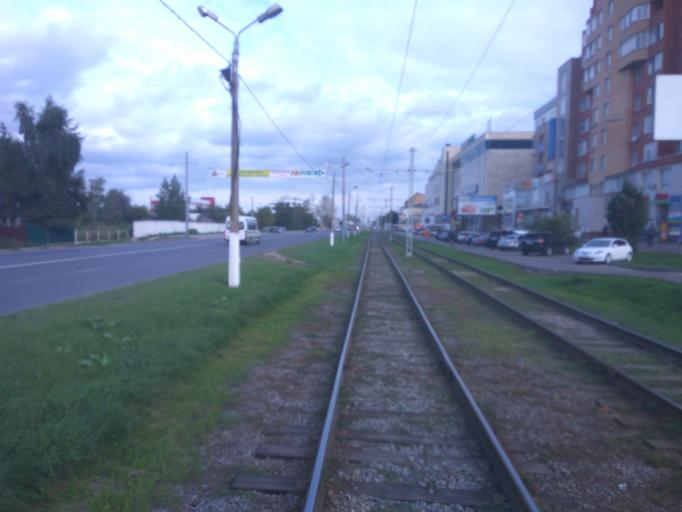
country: RU
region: Moskovskaya
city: Kolomna
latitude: 55.0854
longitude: 38.7982
